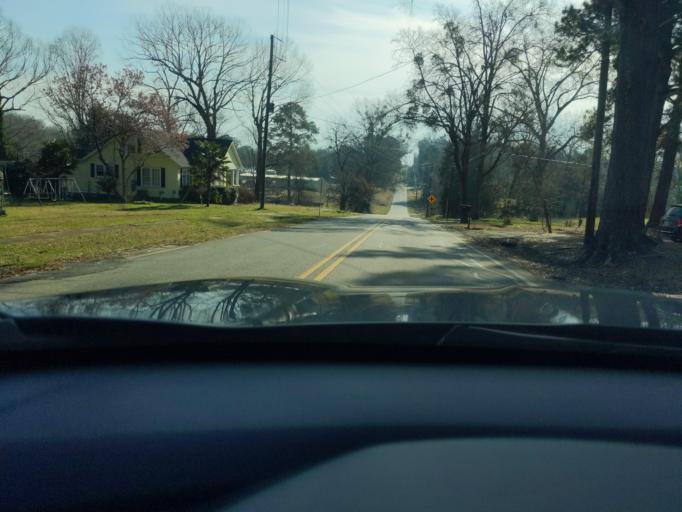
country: US
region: South Carolina
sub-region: Abbeville County
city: Calhoun Falls
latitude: 34.0910
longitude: -82.5959
